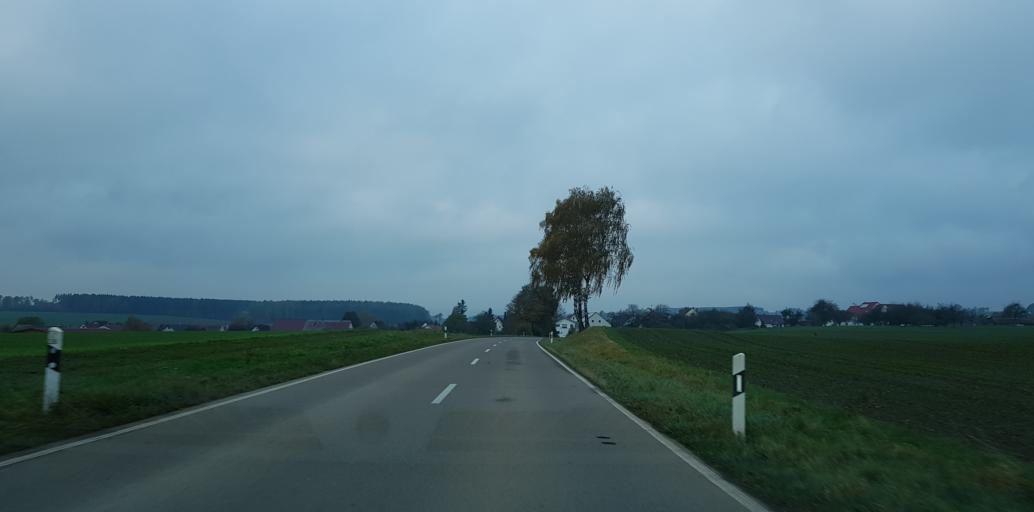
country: DE
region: Baden-Wuerttemberg
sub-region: Tuebingen Region
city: Opfingen
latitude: 48.3101
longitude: 9.7927
